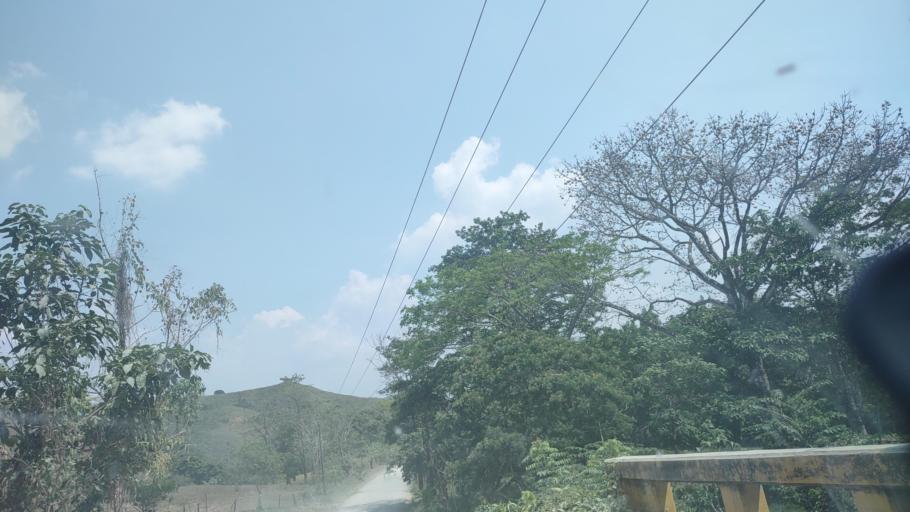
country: MX
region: Tabasco
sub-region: Huimanguillo
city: Francisco Rueda
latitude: 17.5806
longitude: -93.8898
